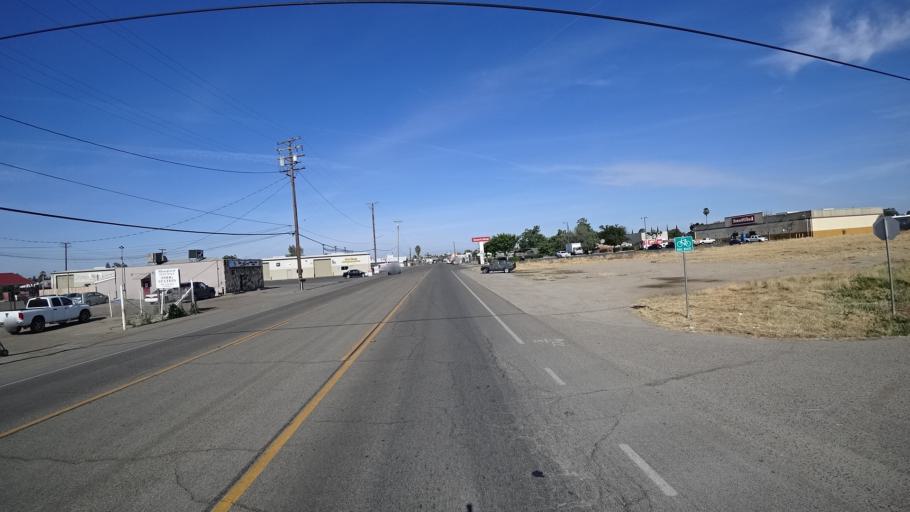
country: US
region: California
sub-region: Kings County
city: Hanford
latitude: 36.3280
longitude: -119.6326
